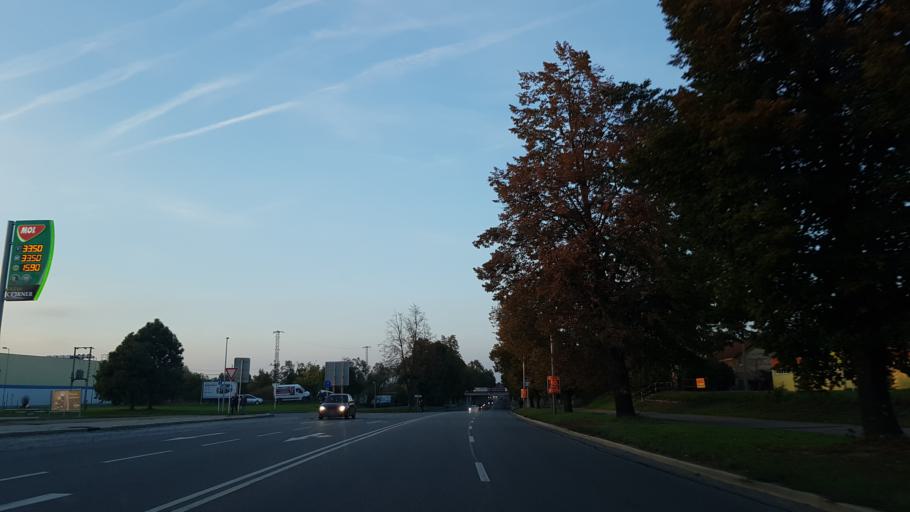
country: CZ
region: Zlin
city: Kunovice
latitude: 49.0502
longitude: 17.4665
